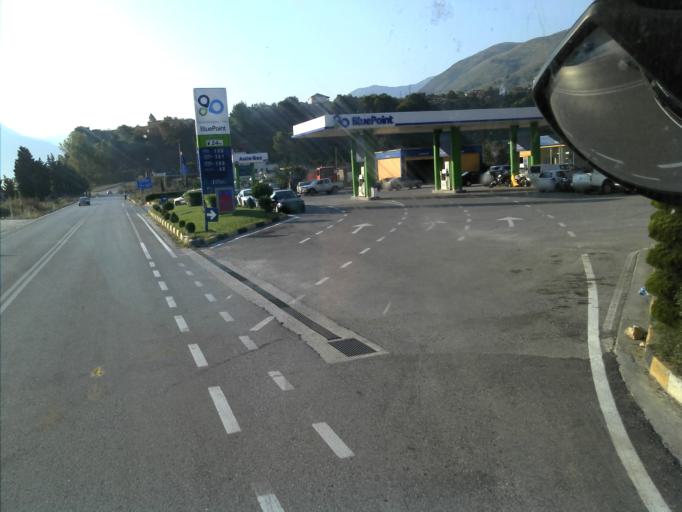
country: AL
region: Gjirokaster
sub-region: Rrethi i Tepelenes
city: Tepelene
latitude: 40.3035
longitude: 20.0193
